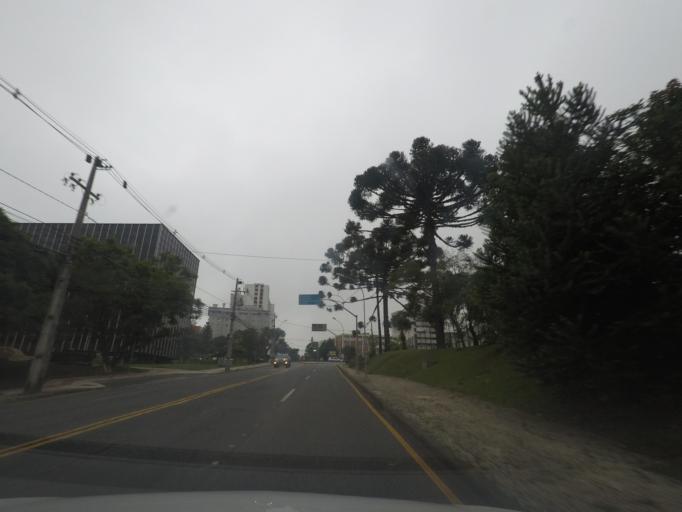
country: BR
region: Parana
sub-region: Curitiba
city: Curitiba
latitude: -25.4124
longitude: -49.2670
